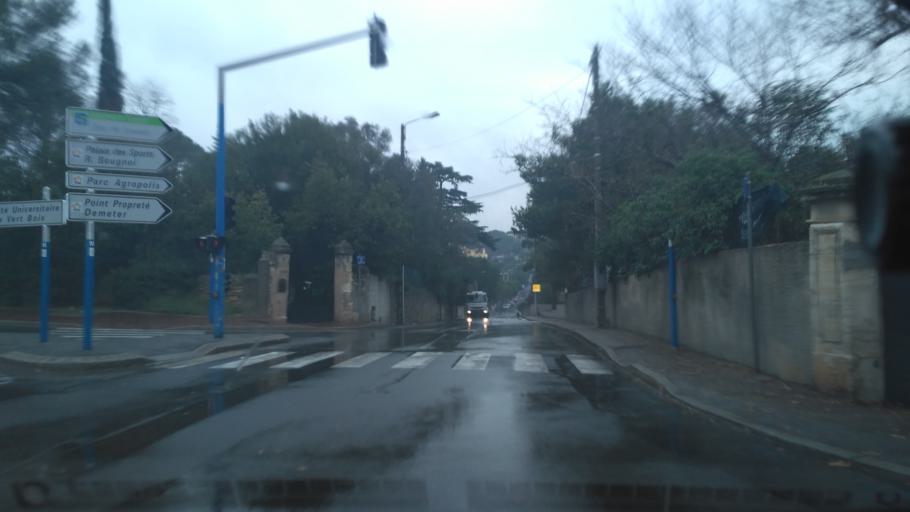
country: FR
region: Languedoc-Roussillon
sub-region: Departement de l'Herault
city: Montpellier
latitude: 43.6346
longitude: 3.8733
